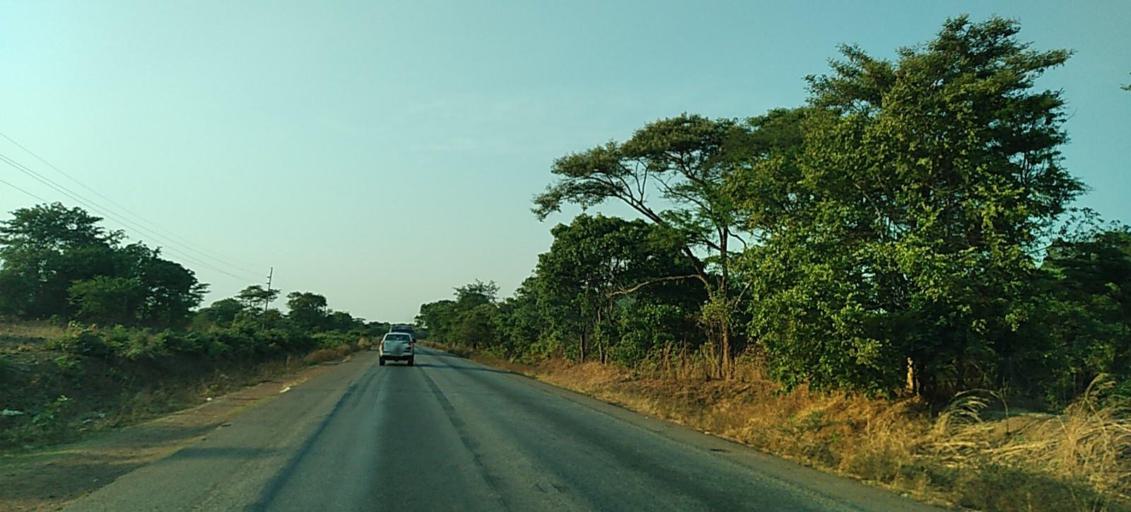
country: ZM
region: Copperbelt
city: Ndola
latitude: -13.1561
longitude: 28.6988
